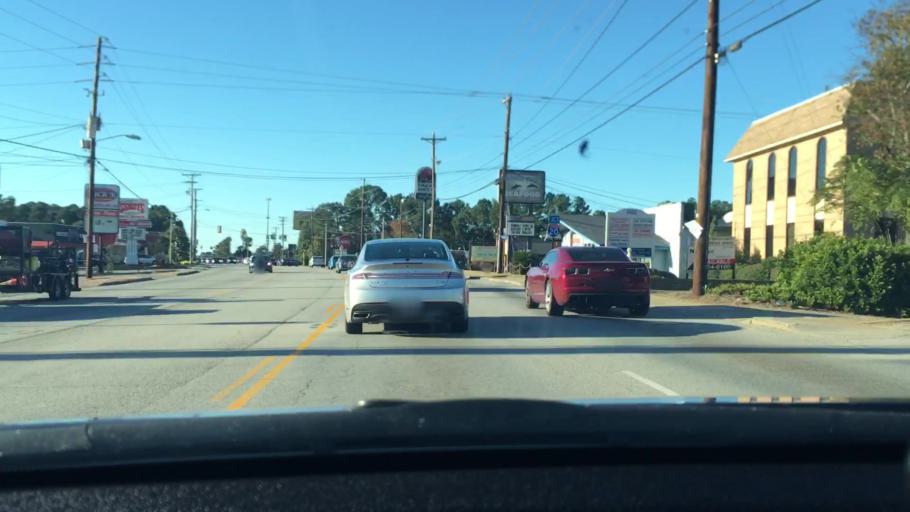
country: US
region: South Carolina
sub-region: Lexington County
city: Saint Andrews
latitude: 34.0360
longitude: -81.0897
